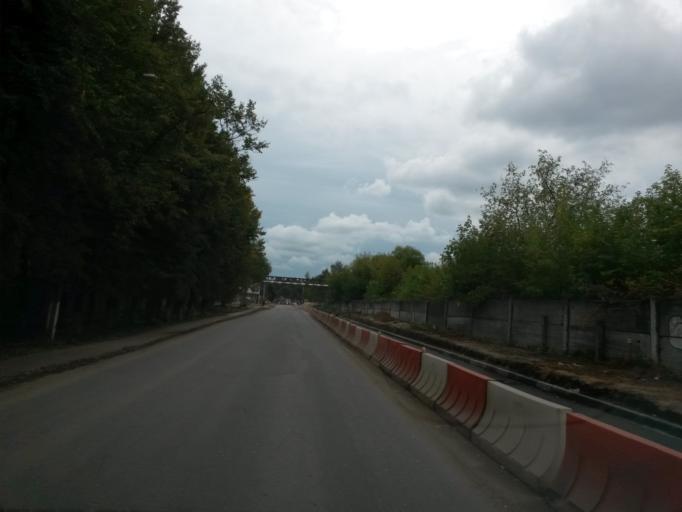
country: RU
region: Moskovskaya
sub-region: Chekhovskiy Rayon
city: Chekhov
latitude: 55.1442
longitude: 37.4746
